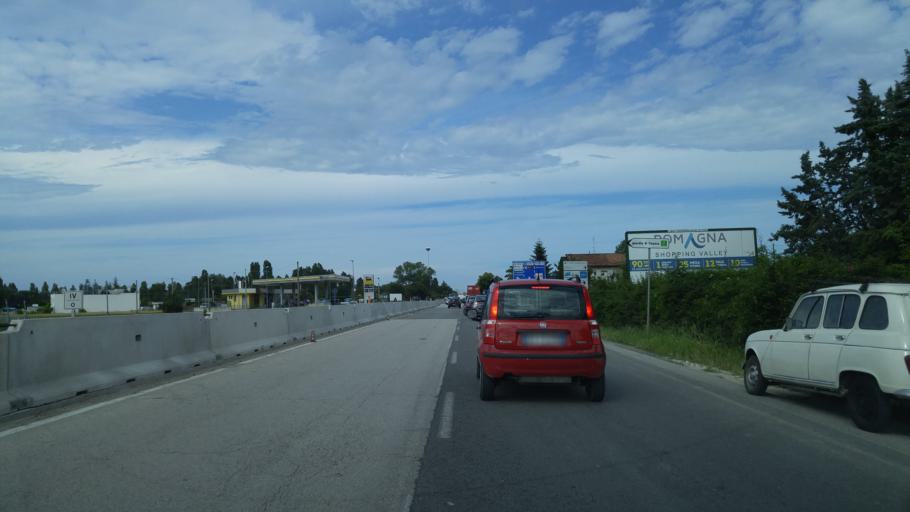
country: IT
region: Emilia-Romagna
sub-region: Provincia di Rimini
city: Rimini
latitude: 44.0393
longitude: 12.5674
